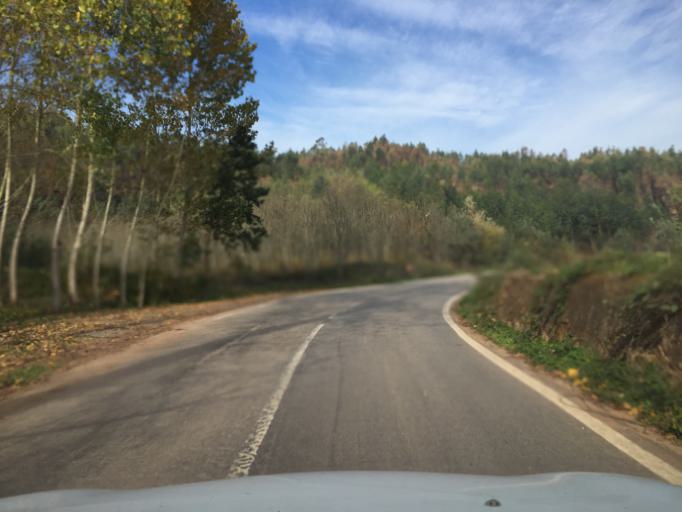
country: PT
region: Aveiro
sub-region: Anadia
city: Anadia
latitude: 40.4147
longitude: -8.4130
